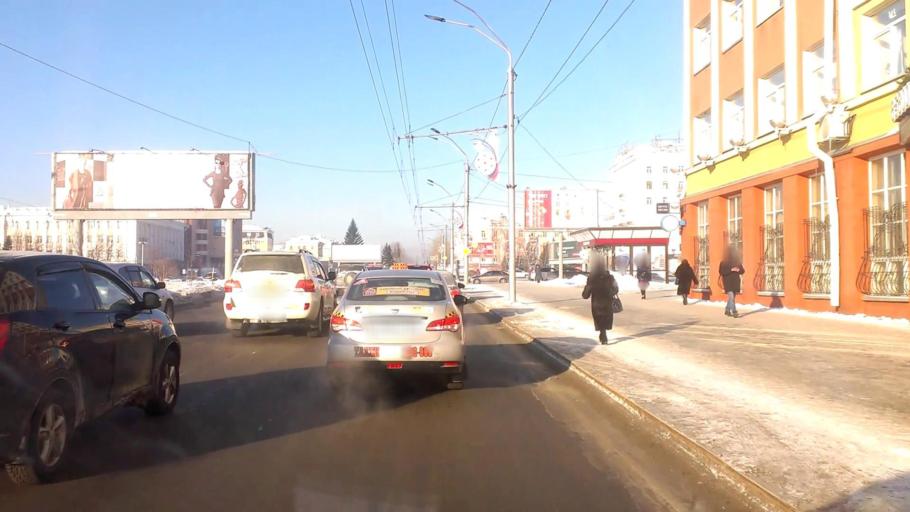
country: RU
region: Altai Krai
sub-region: Gorod Barnaulskiy
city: Barnaul
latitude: 53.3464
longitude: 83.7791
